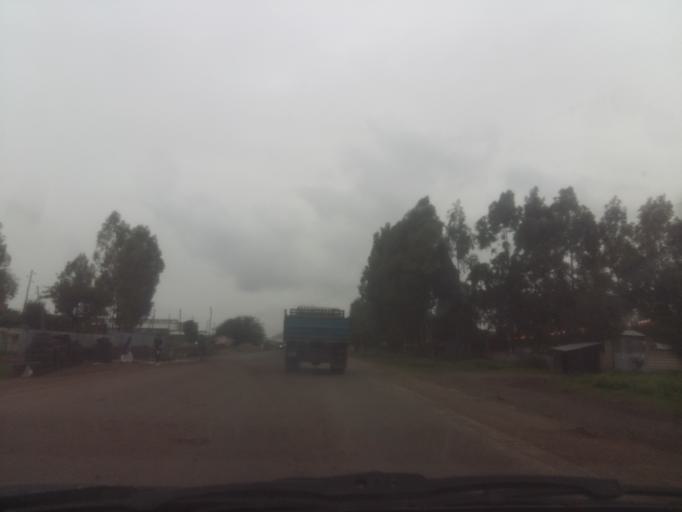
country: ET
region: Oromiya
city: Bishoftu
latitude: 8.8149
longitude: 38.8843
